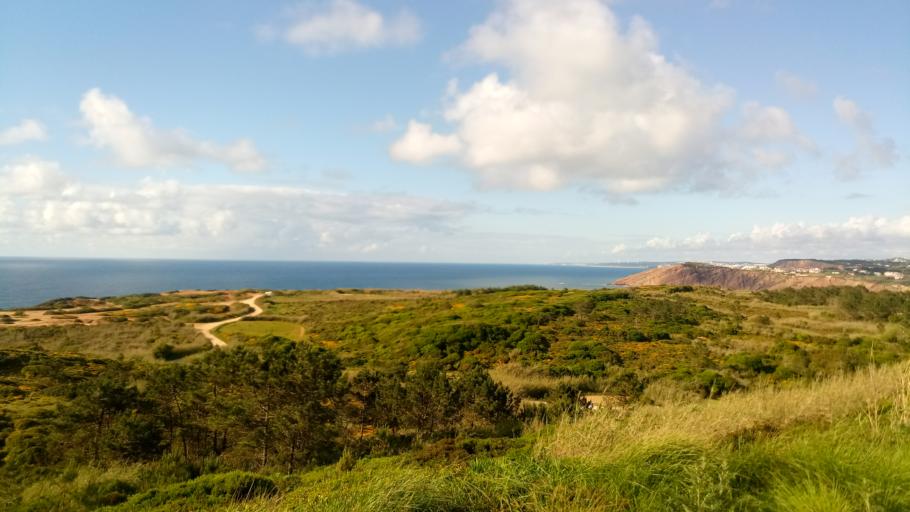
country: PT
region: Leiria
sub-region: Caldas da Rainha
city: Caldas da Rainha
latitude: 39.5006
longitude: -9.1580
